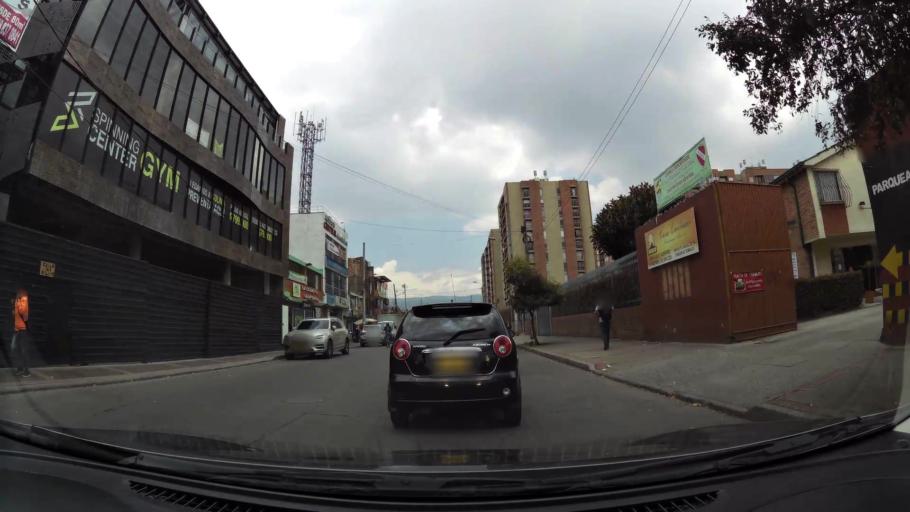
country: CO
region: Cundinamarca
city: Cota
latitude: 4.7502
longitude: -74.0622
